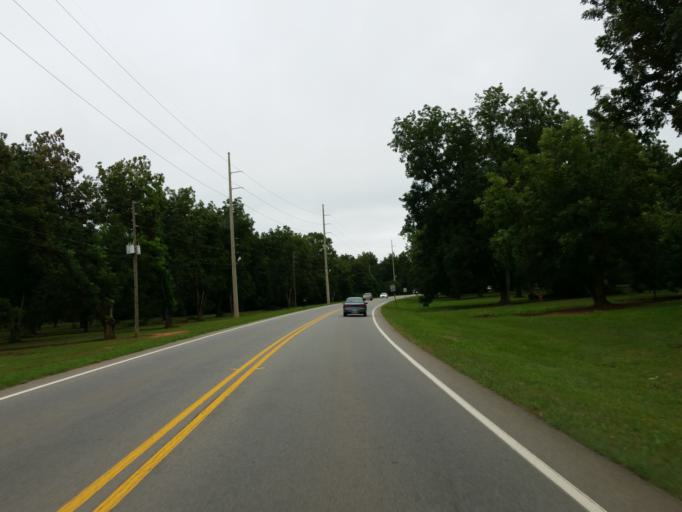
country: US
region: Georgia
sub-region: Peach County
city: Fort Valley
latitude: 32.5719
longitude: -83.8898
